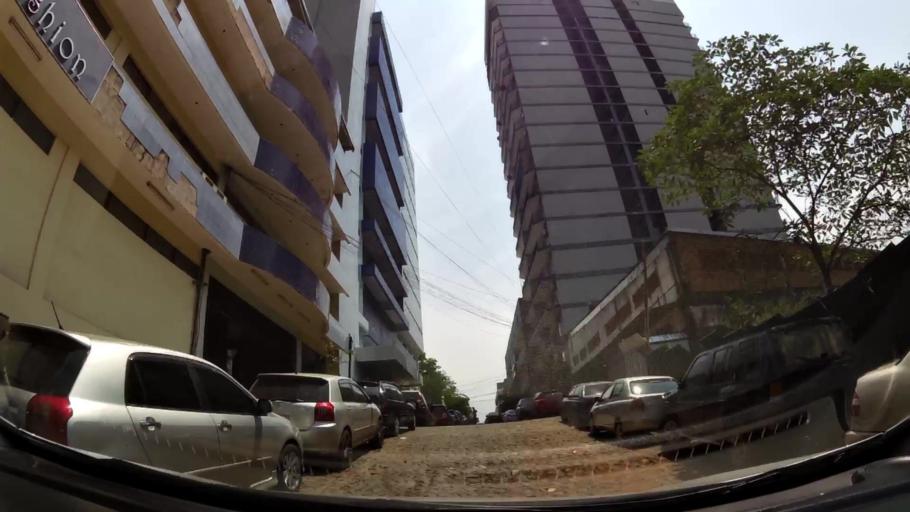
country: PY
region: Alto Parana
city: Ciudad del Este
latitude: -25.5133
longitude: -54.6095
